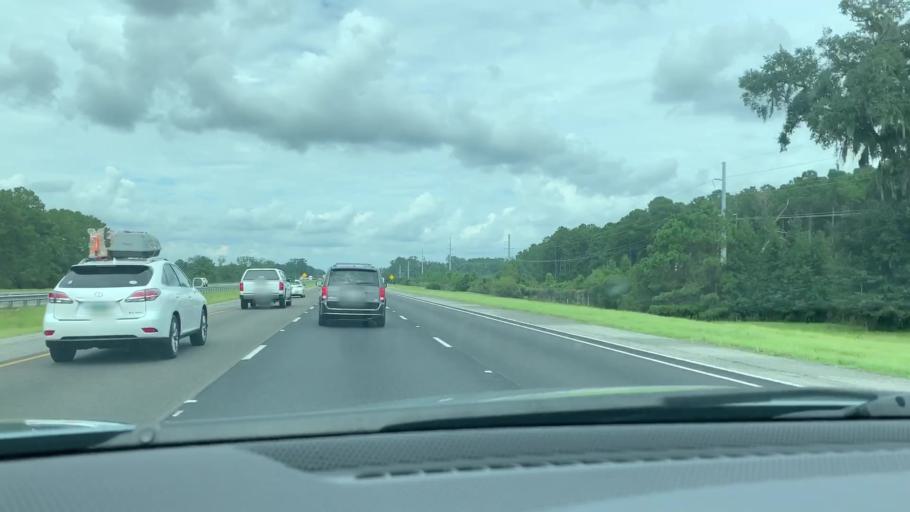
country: US
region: Georgia
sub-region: Liberty County
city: Midway
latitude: 31.8023
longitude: -81.3695
